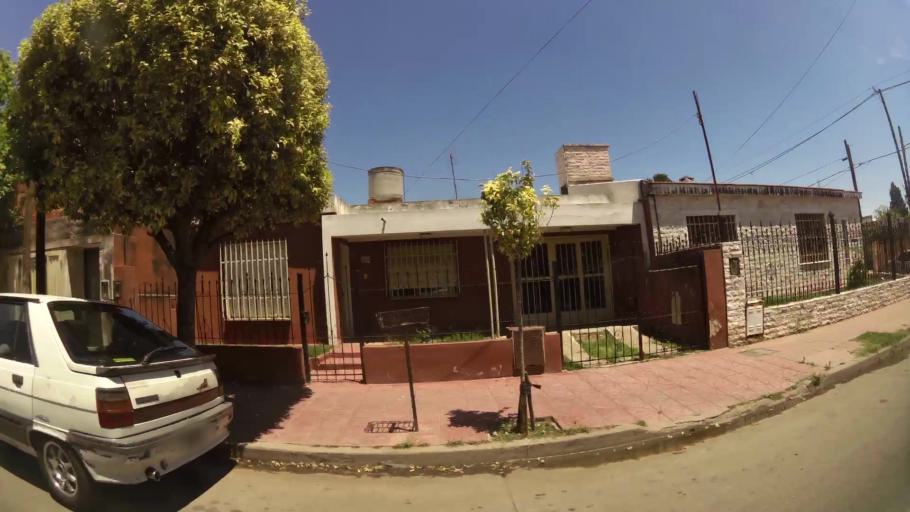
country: AR
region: Cordoba
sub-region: Departamento de Capital
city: Cordoba
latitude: -31.4268
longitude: -64.1256
